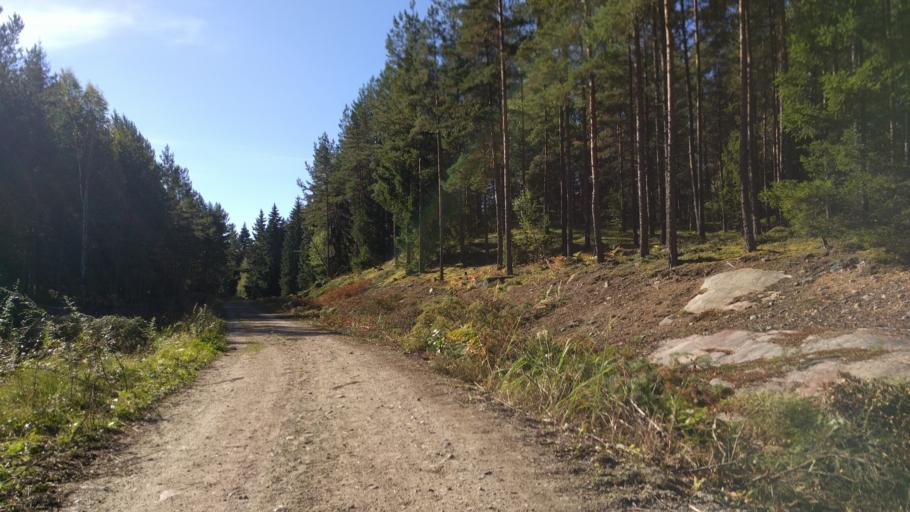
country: SE
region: Stockholm
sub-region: Vallentuna Kommun
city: Vallentuna
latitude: 59.4930
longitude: 18.1129
